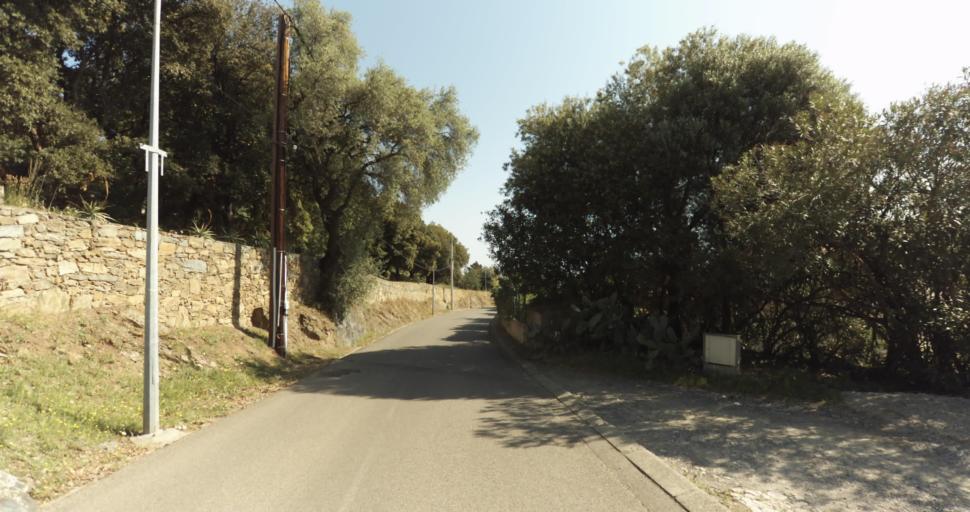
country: FR
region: Corsica
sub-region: Departement de la Haute-Corse
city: Biguglia
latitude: 42.6268
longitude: 9.4223
